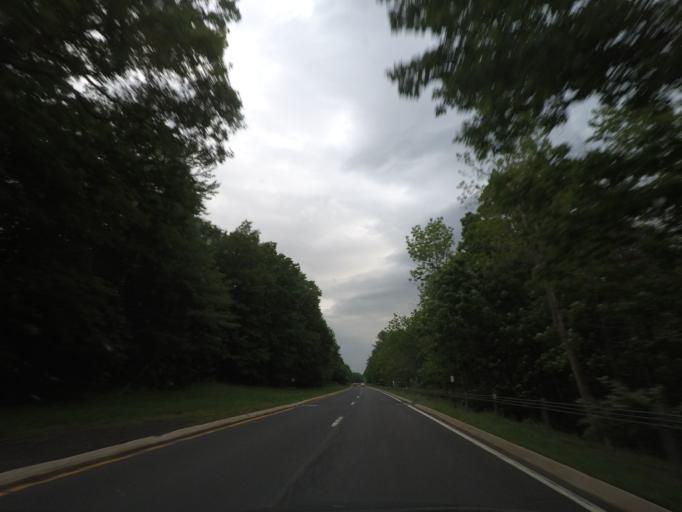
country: US
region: New York
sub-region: Columbia County
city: Philmont
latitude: 42.2383
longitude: -73.6228
